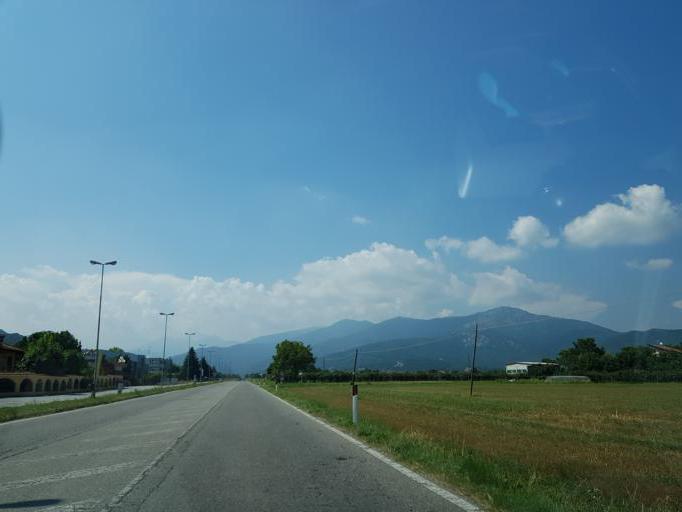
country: IT
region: Piedmont
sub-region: Provincia di Cuneo
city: Montemale di Cuneo
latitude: 44.4471
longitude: 7.3992
